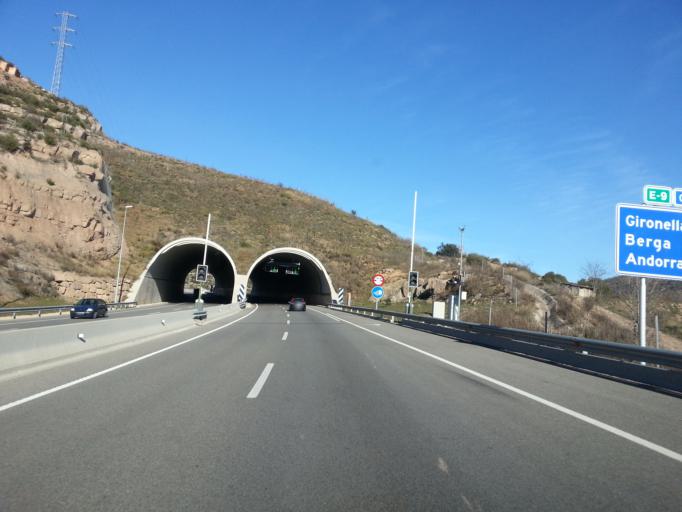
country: ES
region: Catalonia
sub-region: Provincia de Barcelona
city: Puig-reig
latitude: 41.9903
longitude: 1.8846
